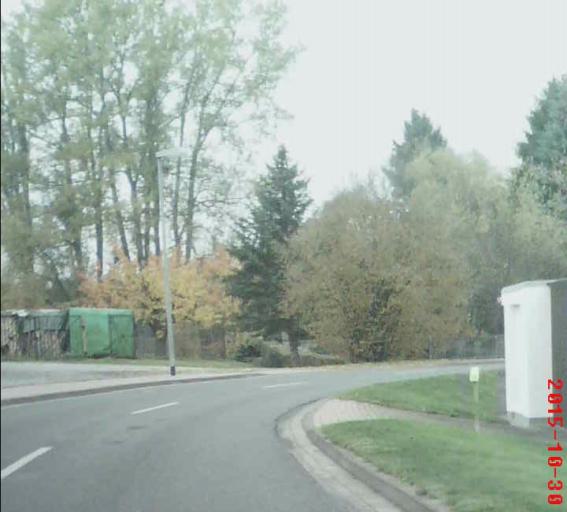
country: DE
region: Thuringia
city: Anrode
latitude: 51.2522
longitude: 10.3428
